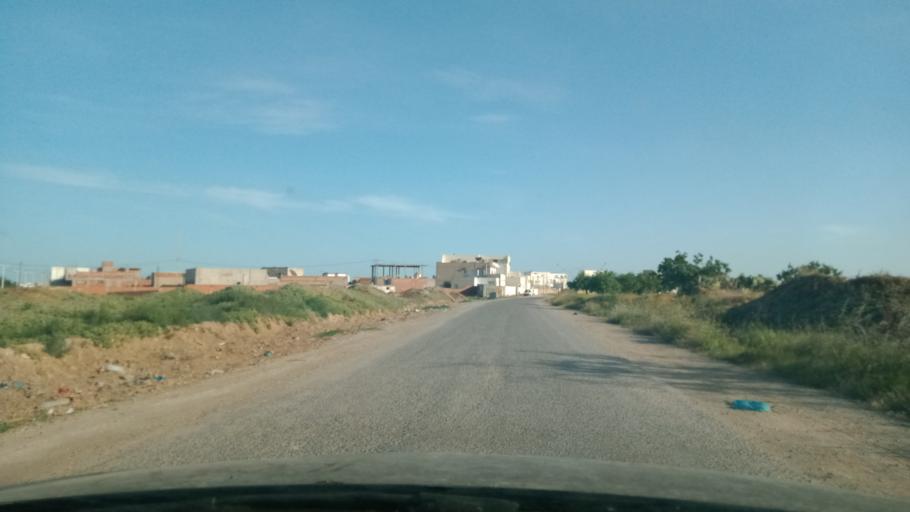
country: TN
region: Safaqis
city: Sfax
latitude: 34.8263
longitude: 10.7356
